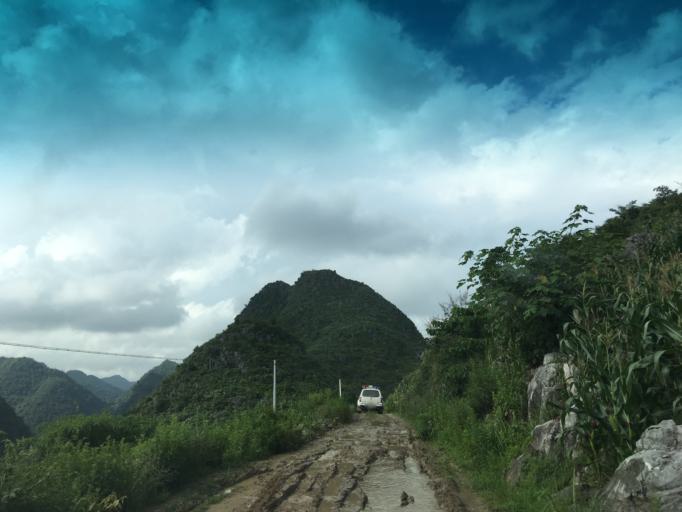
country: CN
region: Guangxi Zhuangzu Zizhiqu
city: Xinzhou
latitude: 24.9911
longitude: 105.6332
